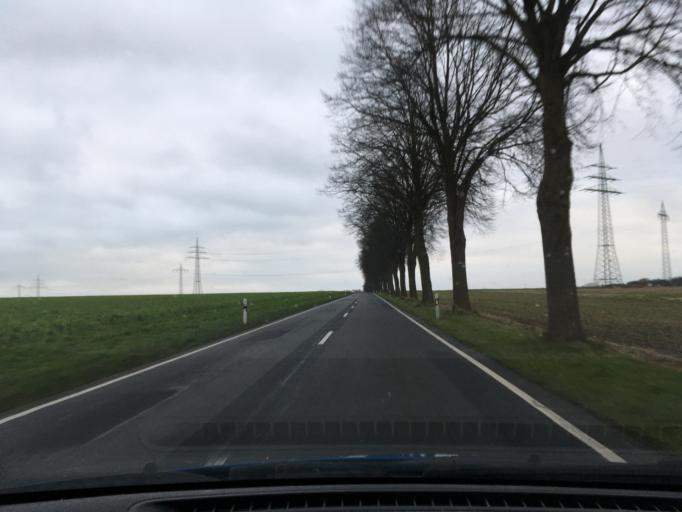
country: DE
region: Lower Saxony
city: Gerdau
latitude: 52.9888
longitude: 10.3927
